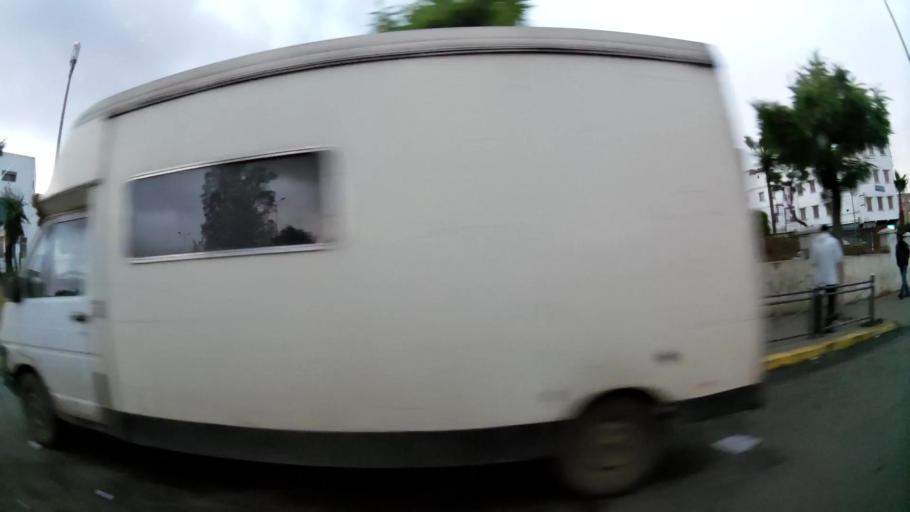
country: MA
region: Grand Casablanca
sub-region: Casablanca
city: Casablanca
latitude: 33.5672
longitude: -7.5998
